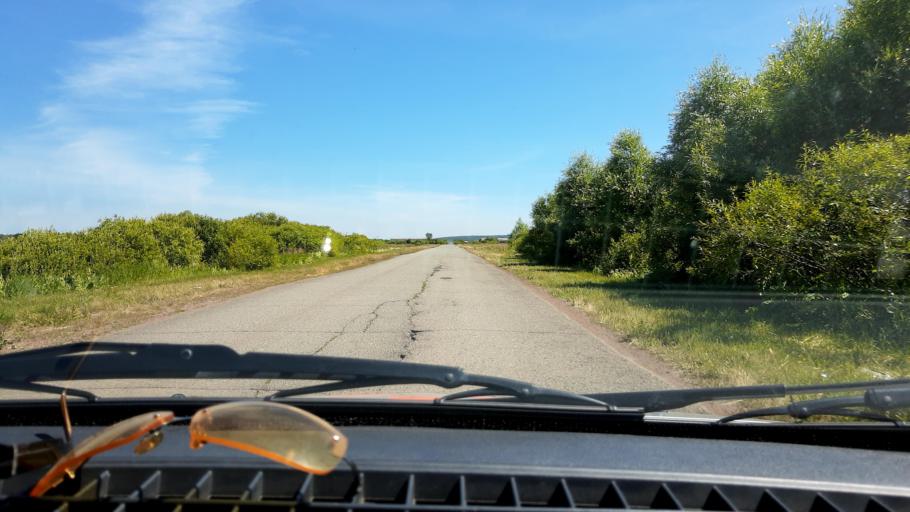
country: RU
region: Bashkortostan
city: Mikhaylovka
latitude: 54.9770
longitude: 55.7761
